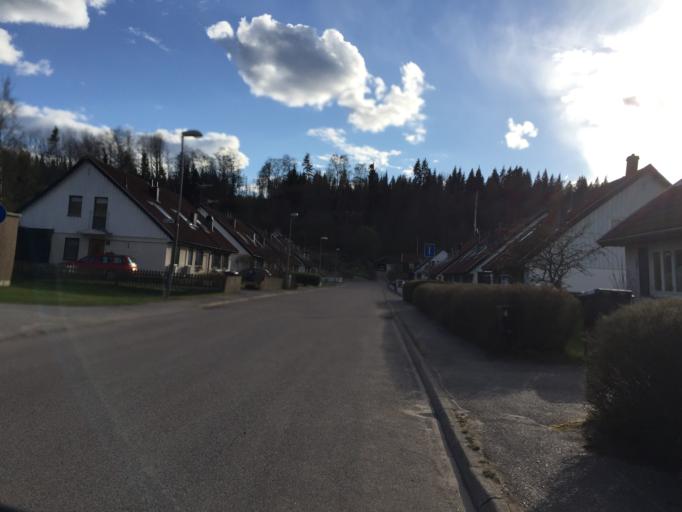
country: SE
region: Dalarna
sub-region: Ludvika Kommun
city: Ludvika
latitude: 60.1261
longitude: 15.1754
